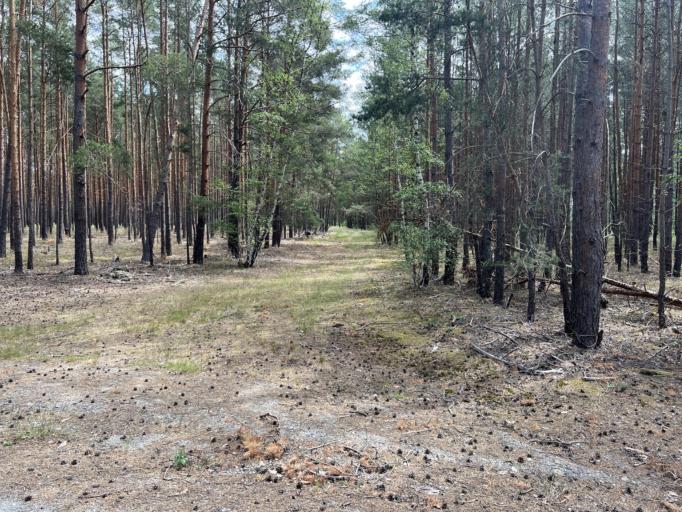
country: DE
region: Brandenburg
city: Gross Koris
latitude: 52.1387
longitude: 13.6606
